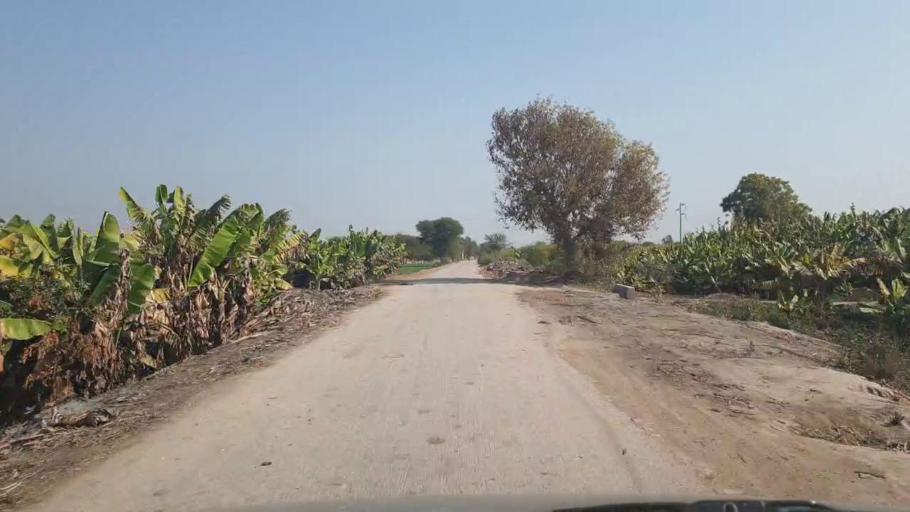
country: PK
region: Sindh
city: Tando Adam
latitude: 25.8203
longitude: 68.6501
